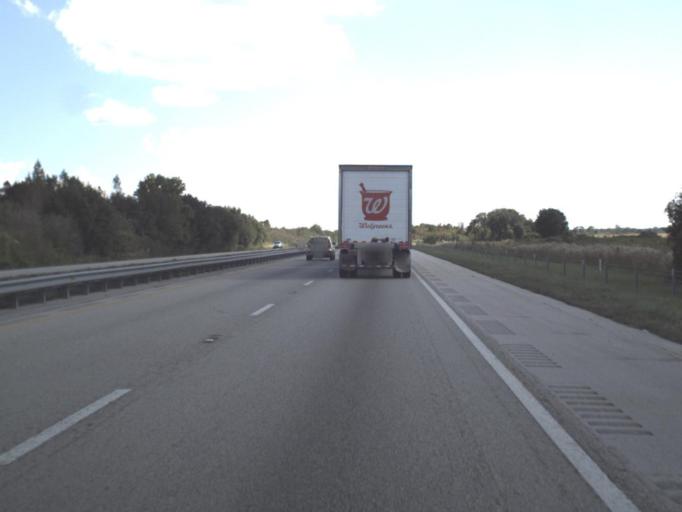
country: US
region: Florida
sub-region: Osceola County
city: Saint Cloud
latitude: 28.0485
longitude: -81.2167
